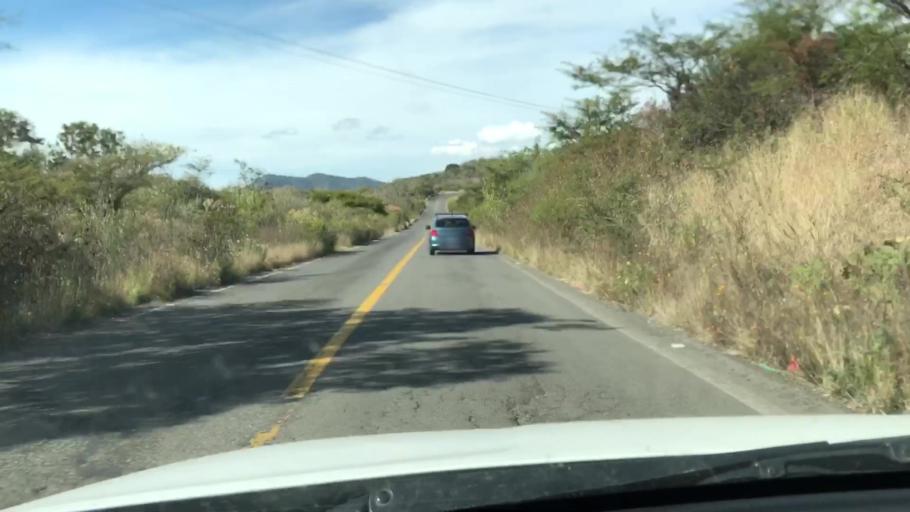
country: MX
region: Jalisco
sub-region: Zacoalco de Torres
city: Barranca de Otates (Barranca de Otatan)
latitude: 20.2087
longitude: -103.6932
